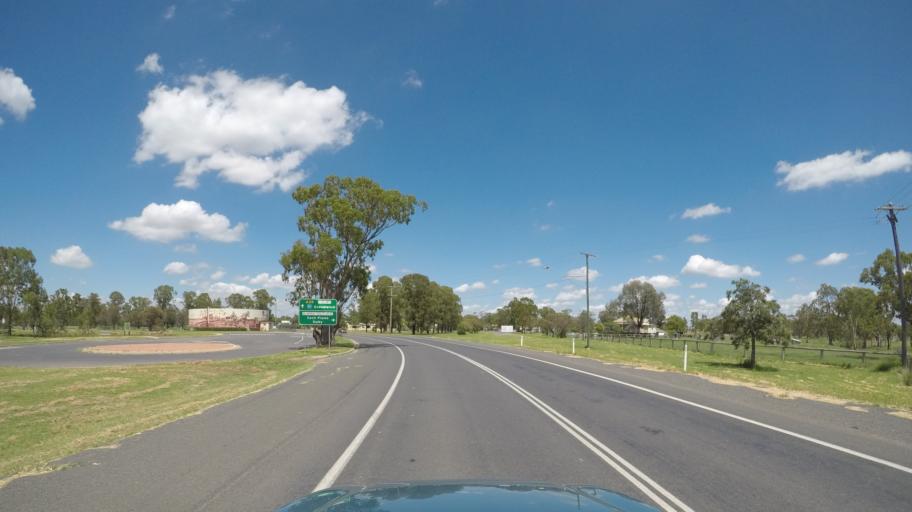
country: AU
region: Queensland
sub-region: Toowoomba
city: Oakey
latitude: -27.8725
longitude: 151.2772
